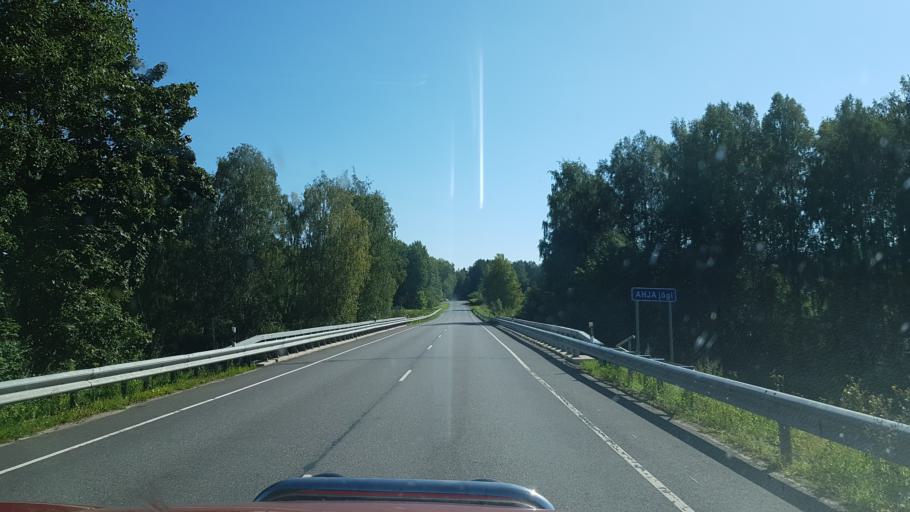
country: EE
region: Polvamaa
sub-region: Polva linn
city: Polva
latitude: 58.2694
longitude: 27.1300
